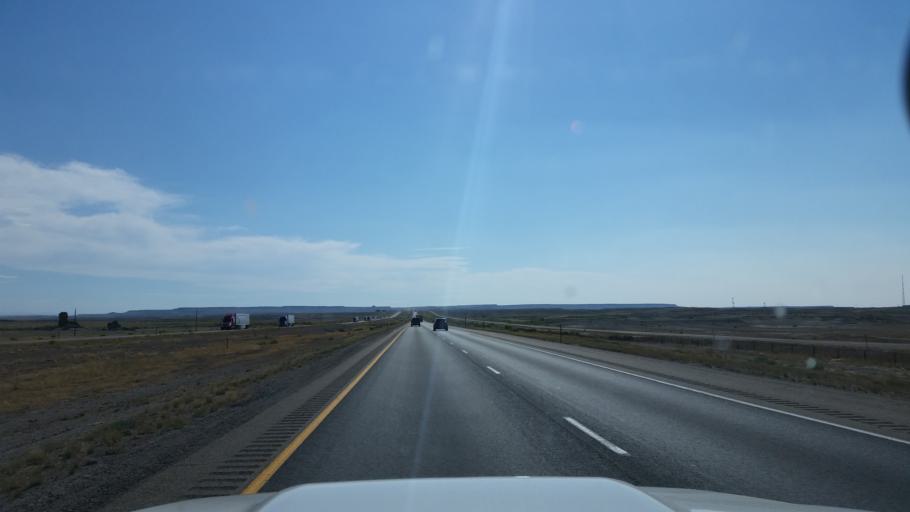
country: US
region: Wyoming
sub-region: Uinta County
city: Lyman
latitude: 41.5368
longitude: -109.9312
